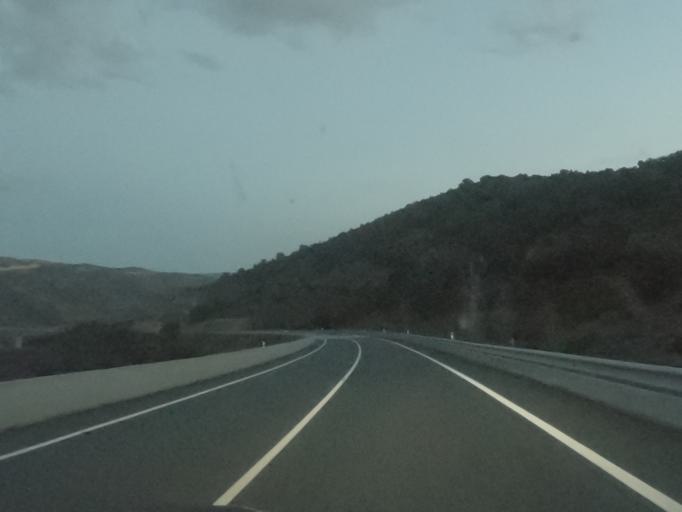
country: PT
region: Braganca
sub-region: Alfandega da Fe
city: Alfandega da Fe
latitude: 41.3121
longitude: -6.9272
